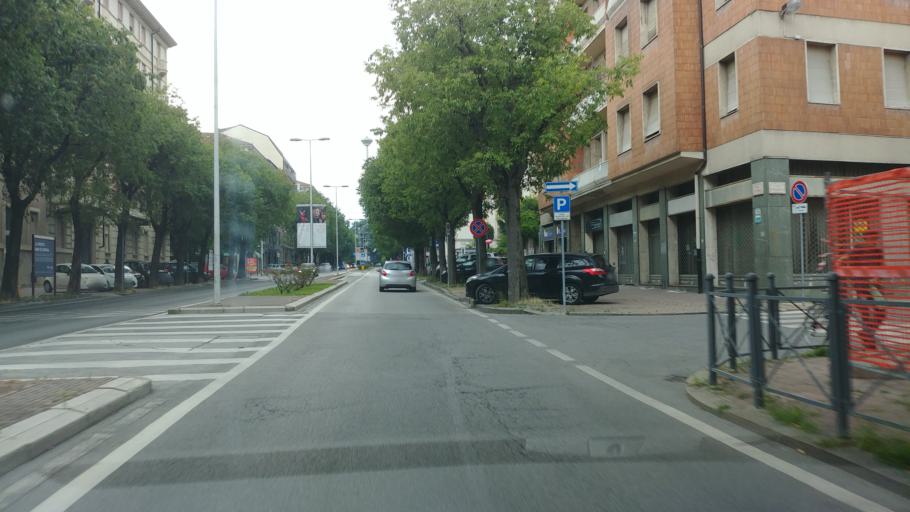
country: IT
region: Piedmont
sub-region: Provincia di Cuneo
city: Cuneo
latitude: 44.3894
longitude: 7.5403
